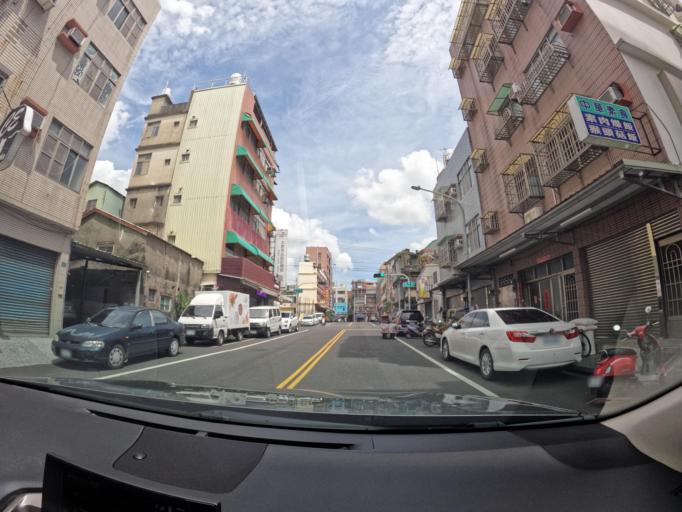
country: TW
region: Kaohsiung
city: Kaohsiung
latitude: 22.6870
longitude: 120.2903
